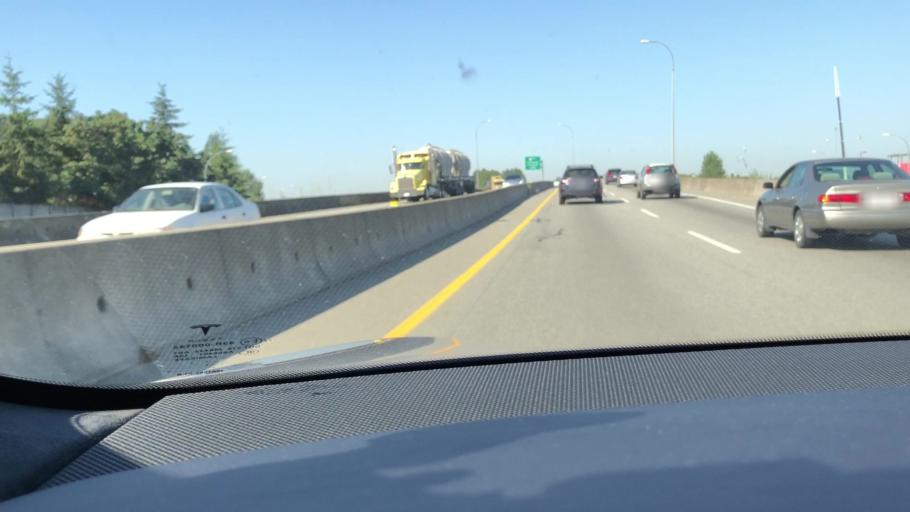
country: CA
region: British Columbia
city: New Westminster
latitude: 49.1886
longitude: -122.9457
